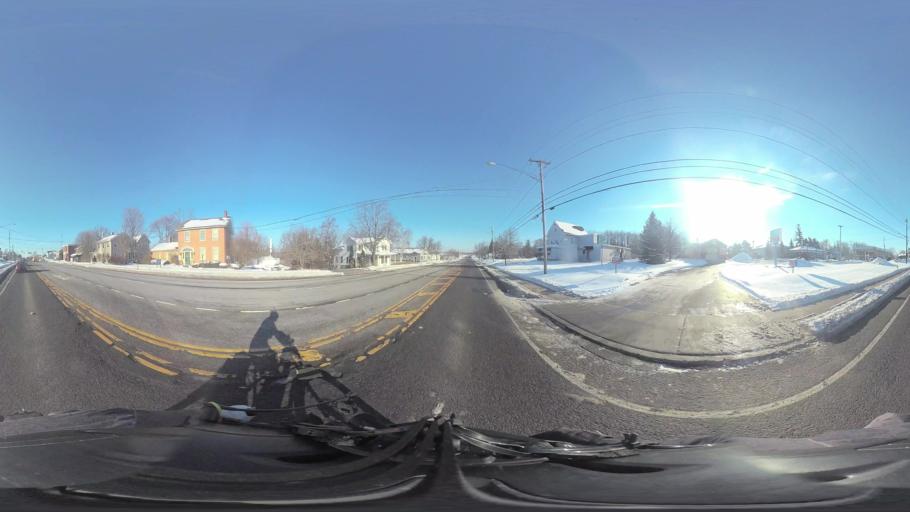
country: US
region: New York
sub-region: Monroe County
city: Rochester
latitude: 43.0633
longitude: -77.6104
